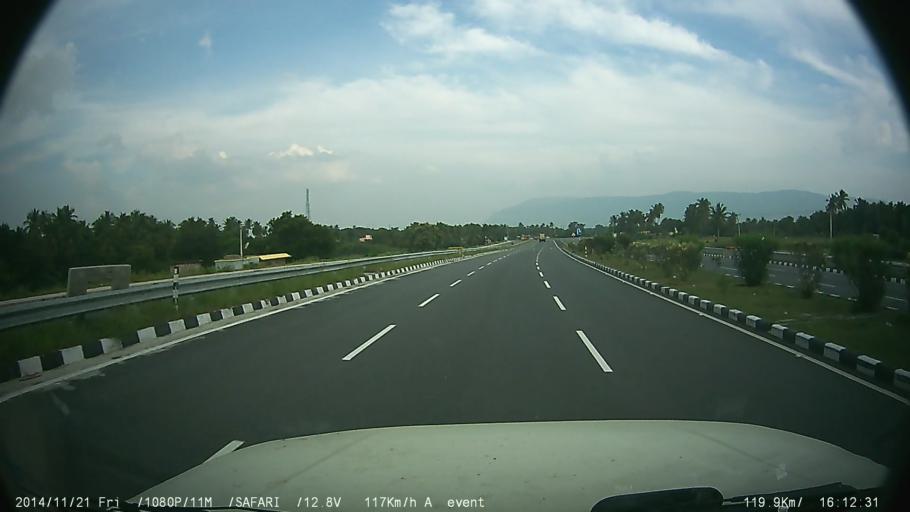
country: IN
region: Tamil Nadu
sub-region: Vellore
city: Jolarpettai
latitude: 12.5972
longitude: 78.5269
